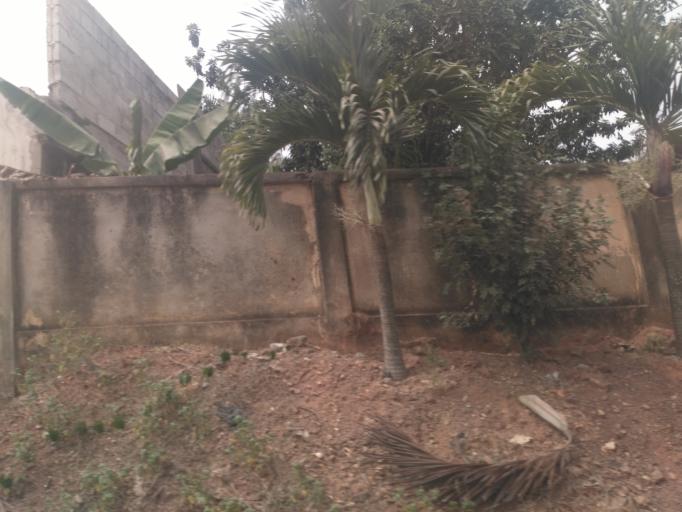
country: GH
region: Ashanti
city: Kumasi
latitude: 6.6721
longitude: -1.6160
